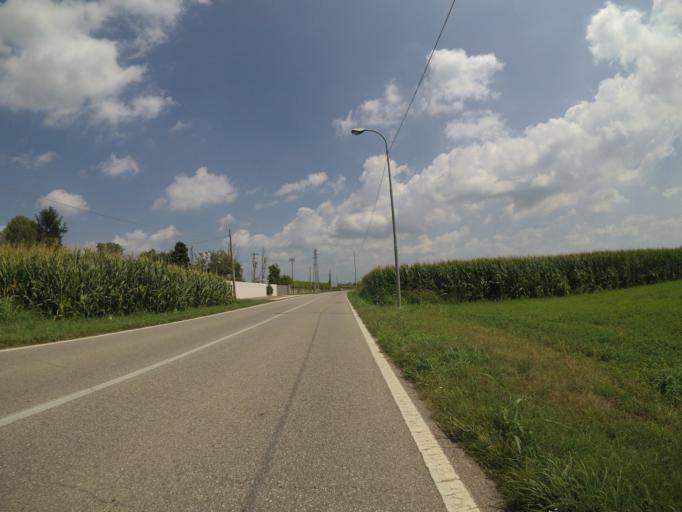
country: IT
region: Friuli Venezia Giulia
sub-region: Provincia di Udine
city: Mereto di Tomba
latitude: 46.0253
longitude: 13.0455
